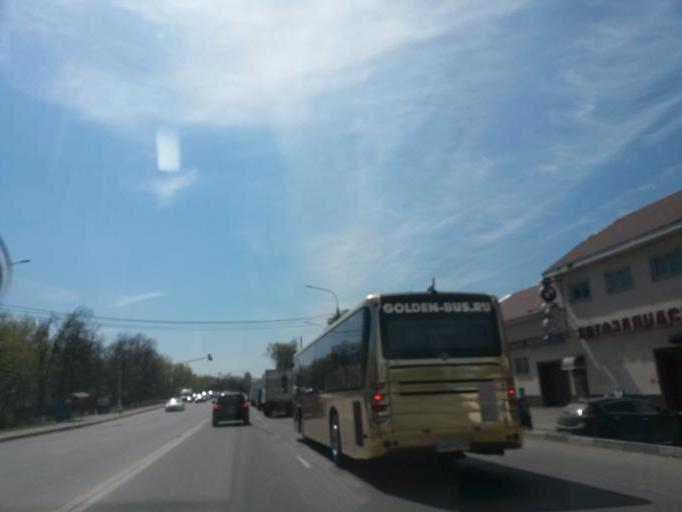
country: RU
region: Moskovskaya
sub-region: Podol'skiy Rayon
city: Podol'sk
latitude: 55.4614
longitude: 37.5592
